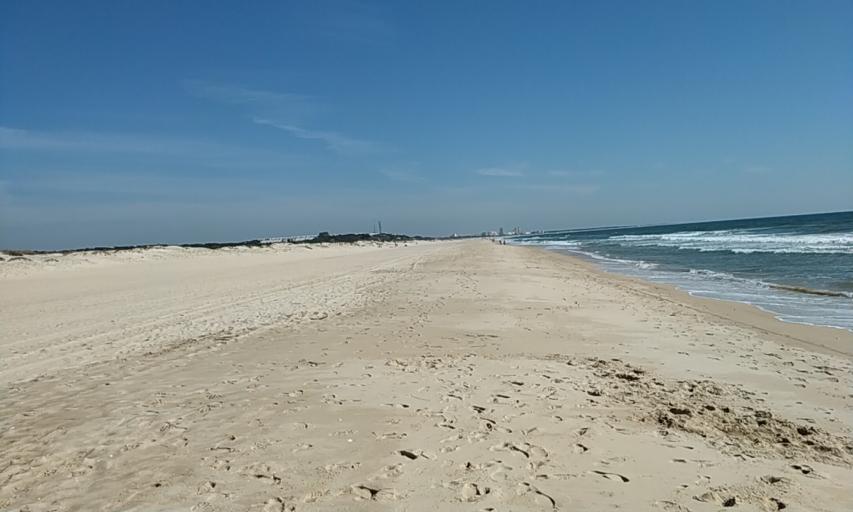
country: PT
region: Faro
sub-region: Vila Real de Santo Antonio
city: Monte Gordo
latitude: 37.1700
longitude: -7.4954
